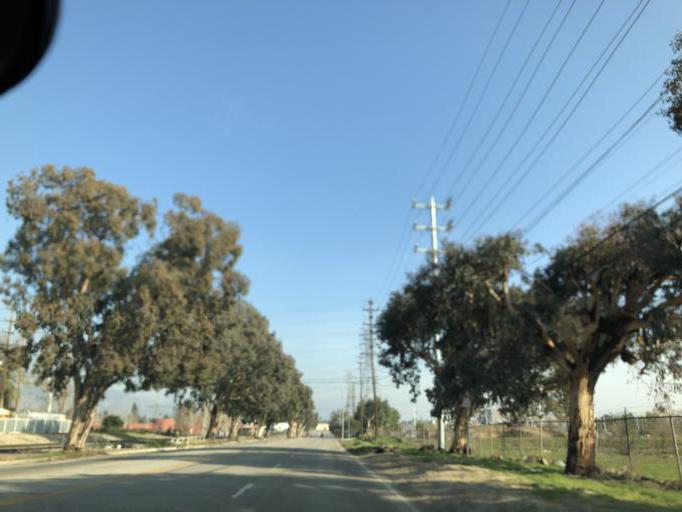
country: US
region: California
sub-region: Los Angeles County
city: San Fernando
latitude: 34.3144
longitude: -118.4869
